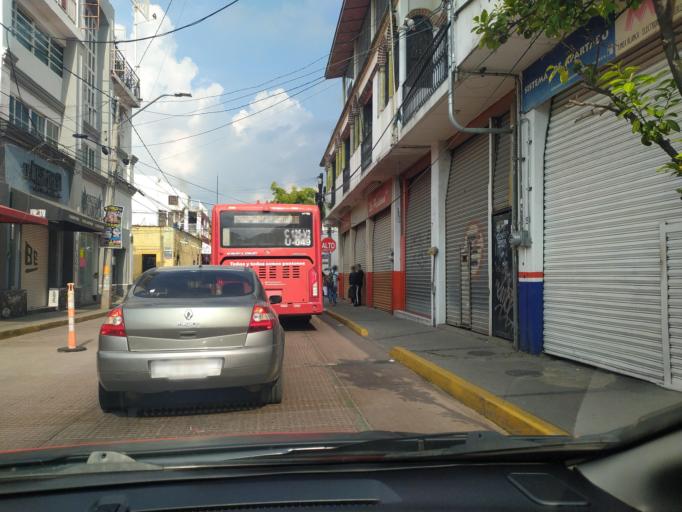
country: MX
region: Jalisco
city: Tlajomulco de Zuniga
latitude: 20.4763
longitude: -103.4478
